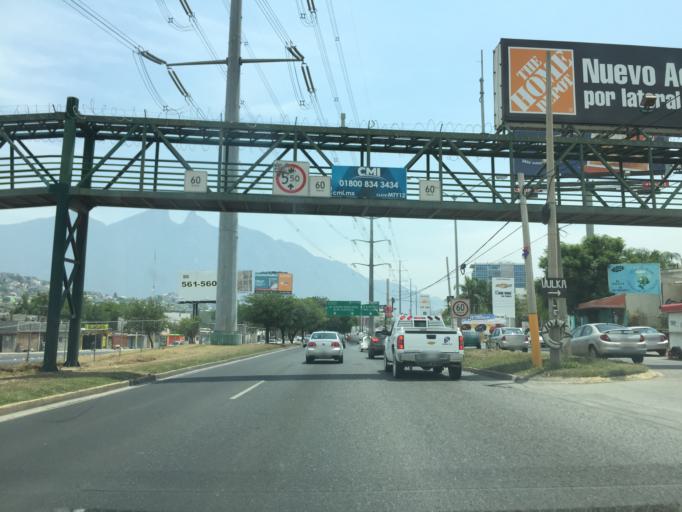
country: MX
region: Nuevo Leon
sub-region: Monterrey
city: Monterrey
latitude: 25.6338
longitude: -100.3054
